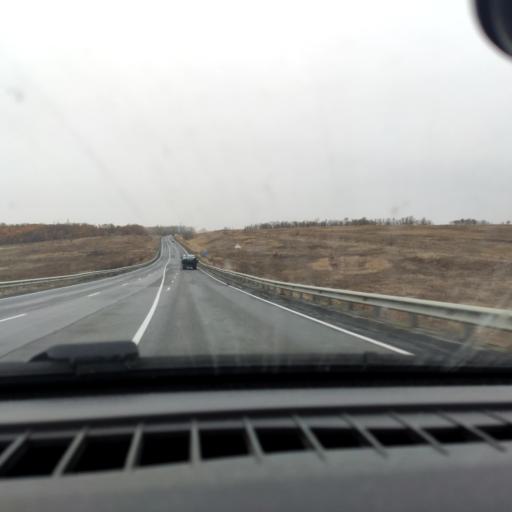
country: RU
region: Voronezj
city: Ostrogozhsk
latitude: 50.9360
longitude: 39.0565
